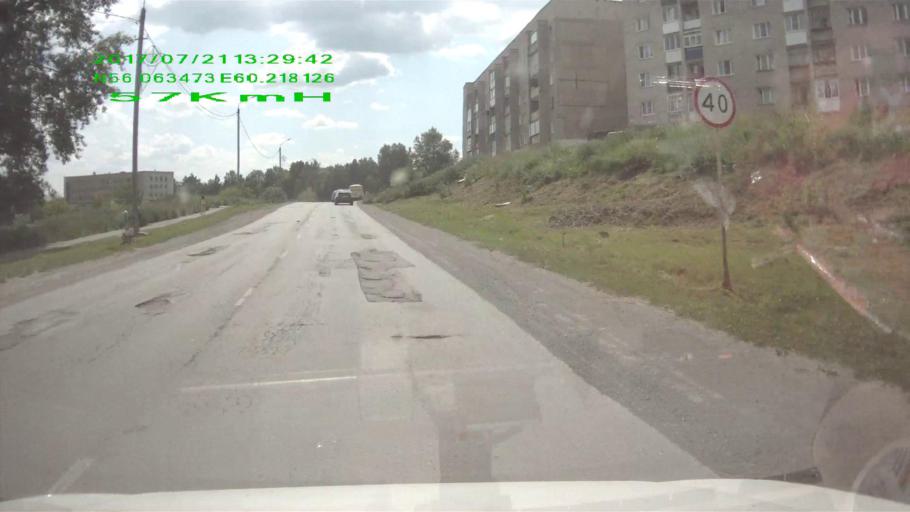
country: RU
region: Chelyabinsk
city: Verkhniy Ufaley
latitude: 56.0623
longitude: 60.2180
